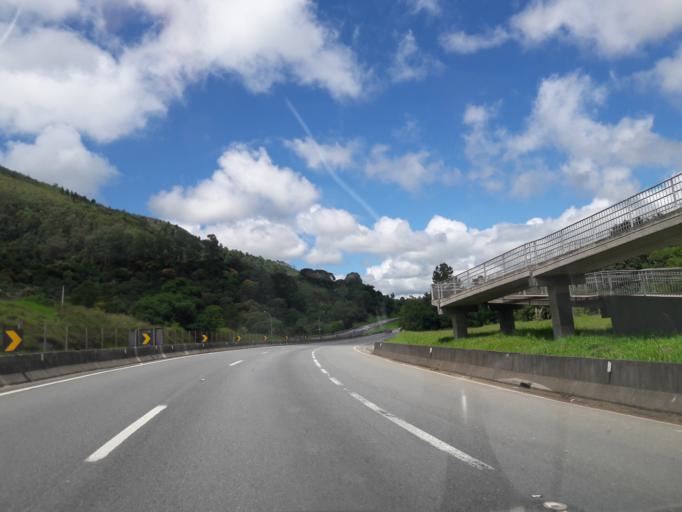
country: BR
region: Parana
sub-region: Campina Grande Do Sul
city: Campina Grande do Sul
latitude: -25.1401
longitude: -48.8561
